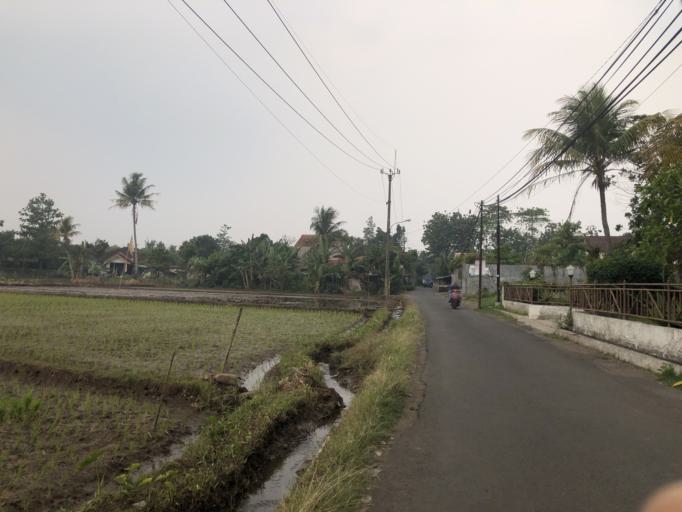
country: ID
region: West Java
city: Ciampea
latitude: -6.5674
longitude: 106.7459
